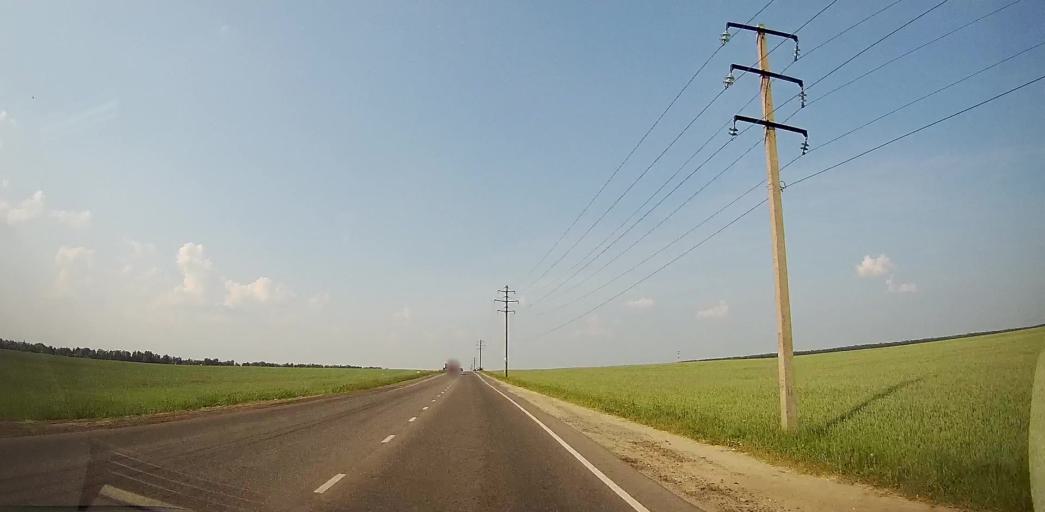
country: RU
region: Moskovskaya
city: Barybino
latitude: 55.2526
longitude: 37.9186
